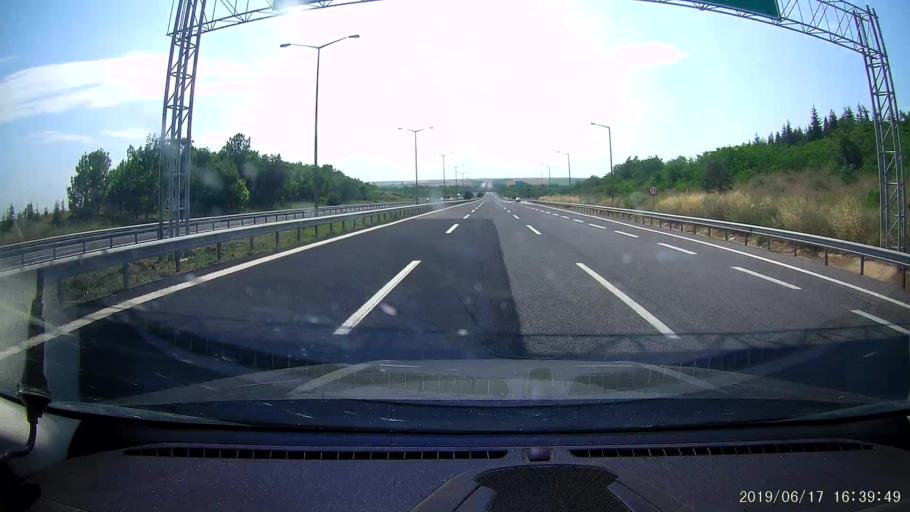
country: TR
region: Kirklareli
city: Luleburgaz
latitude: 41.4499
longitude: 27.3986
